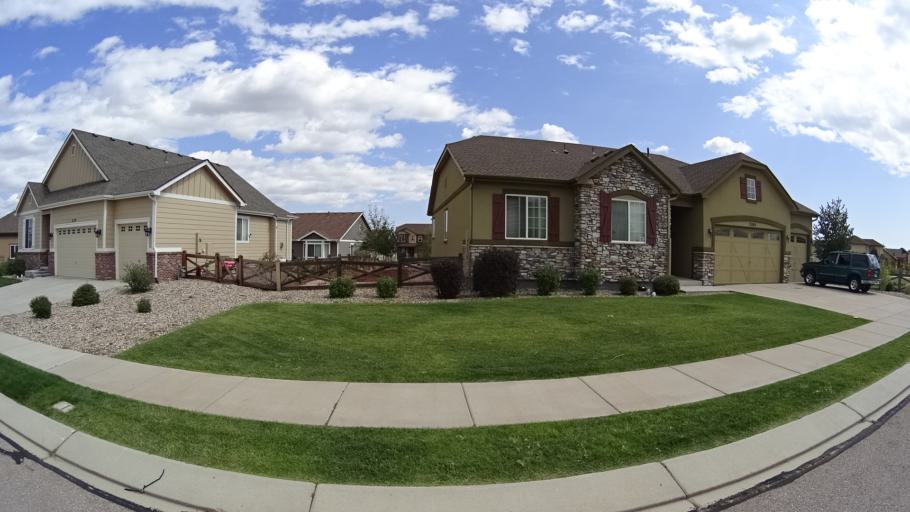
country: US
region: Colorado
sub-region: El Paso County
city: Cimarron Hills
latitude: 38.9349
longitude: -104.6788
